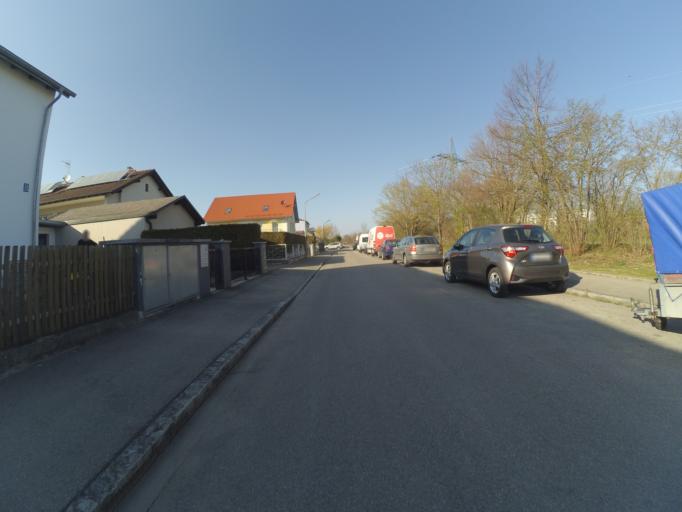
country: DE
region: Bavaria
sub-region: Upper Bavaria
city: Oberschleissheim
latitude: 48.2172
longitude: 11.5473
